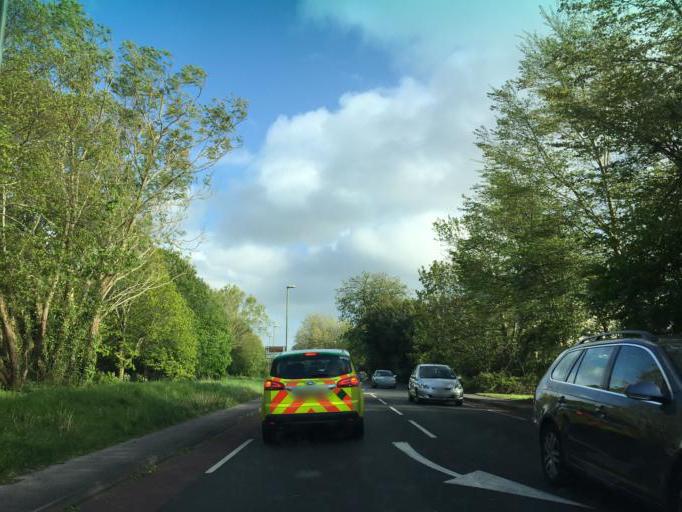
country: GB
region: England
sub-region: Hampshire
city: Fareham
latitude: 50.8294
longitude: -1.1677
